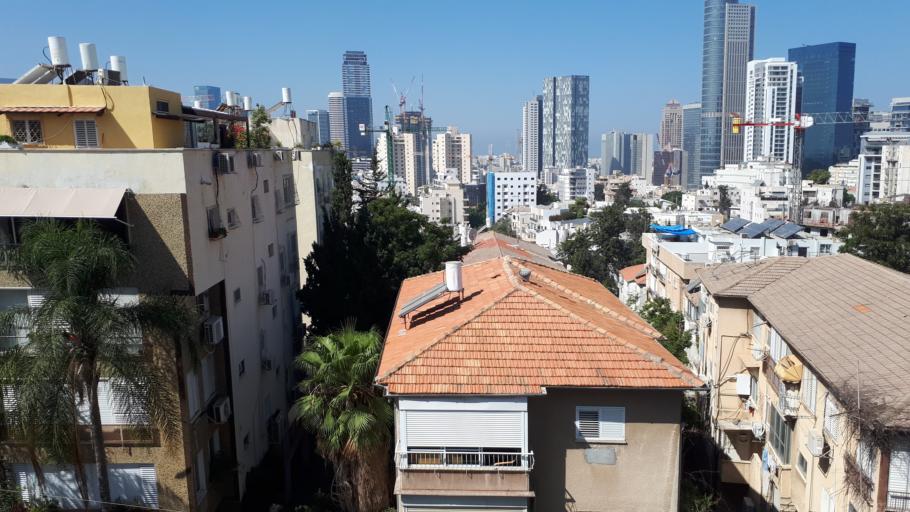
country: IL
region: Tel Aviv
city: Ramat Gan
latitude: 32.0798
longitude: 34.8111
